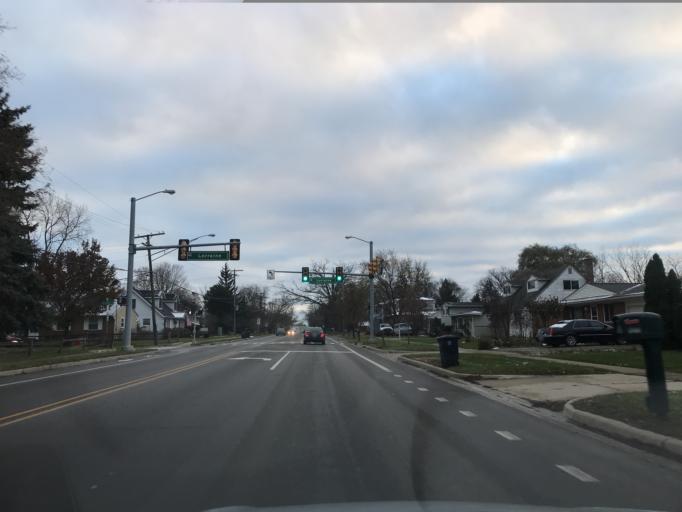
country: US
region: Michigan
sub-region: Washtenaw County
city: Ann Arbor
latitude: 42.2388
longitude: -83.7001
